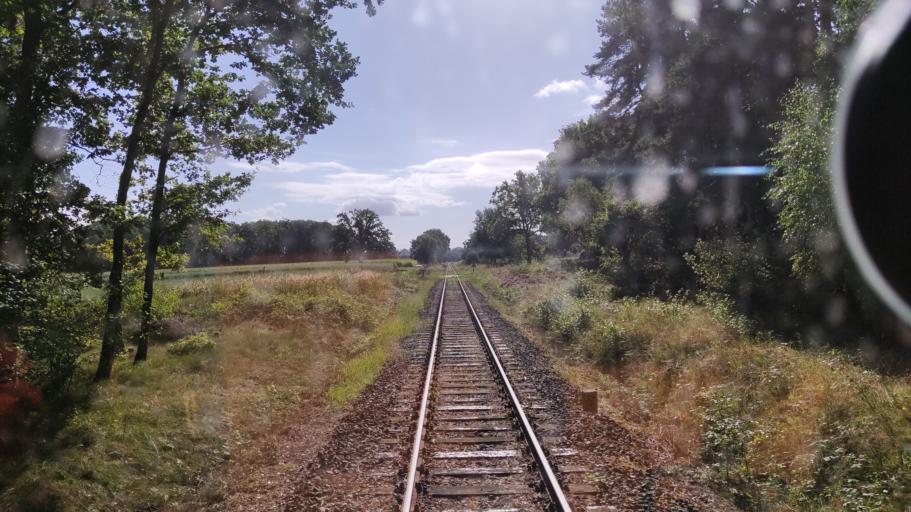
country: DE
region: Lower Saxony
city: Neetze
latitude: 53.2743
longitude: 10.6084
